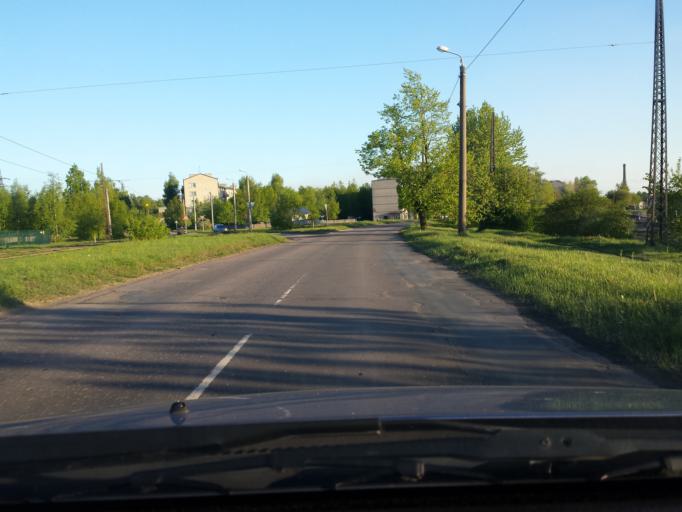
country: LV
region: Riga
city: Jaunciems
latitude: 57.0112
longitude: 24.1246
